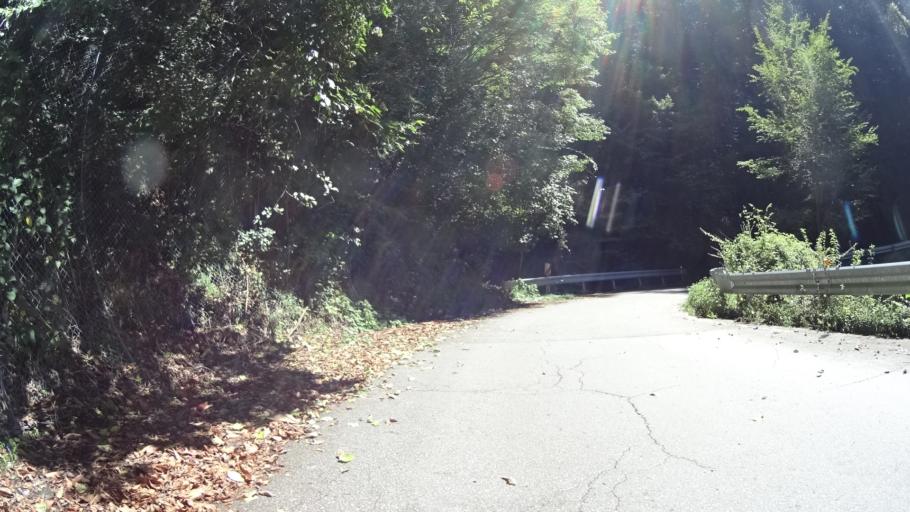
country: JP
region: Yamanashi
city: Enzan
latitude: 35.7435
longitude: 138.8223
